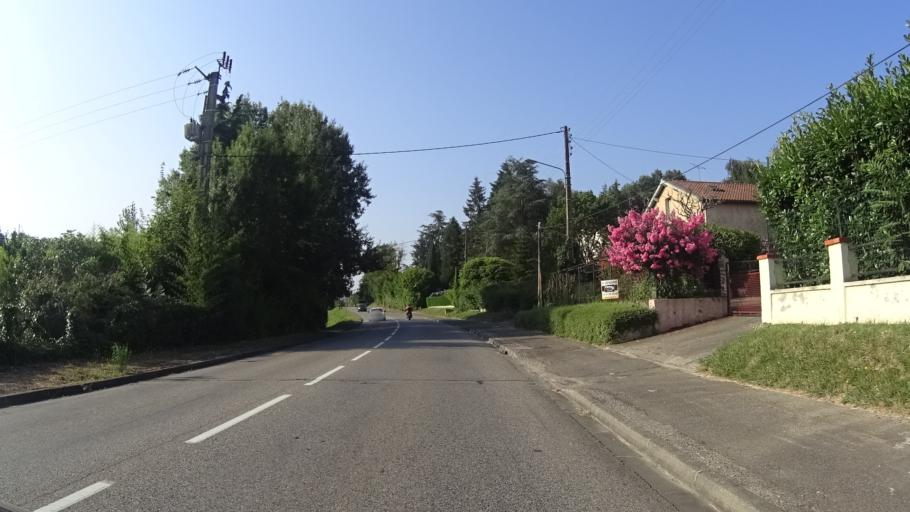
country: FR
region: Midi-Pyrenees
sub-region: Departement de l'Ariege
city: Mirepoix
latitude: 43.0798
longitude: 1.8766
